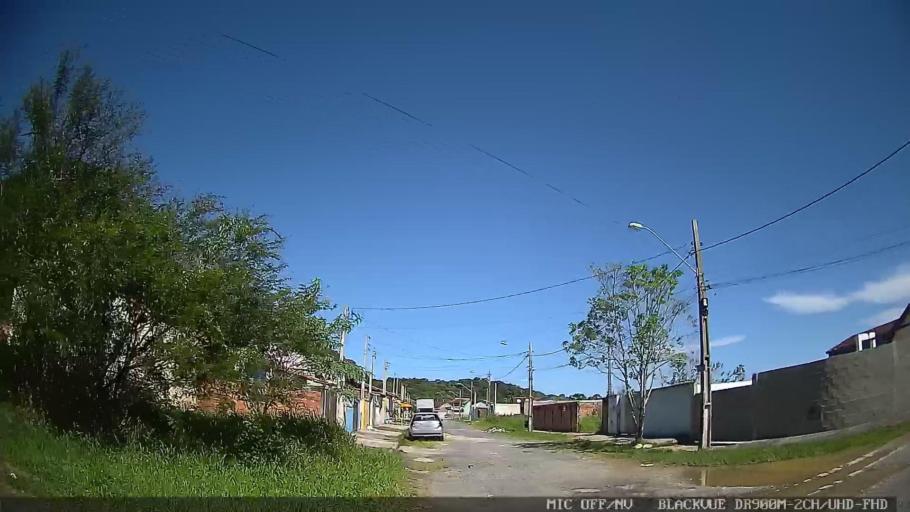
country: BR
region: Sao Paulo
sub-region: Iguape
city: Iguape
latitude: -24.6940
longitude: -47.5595
